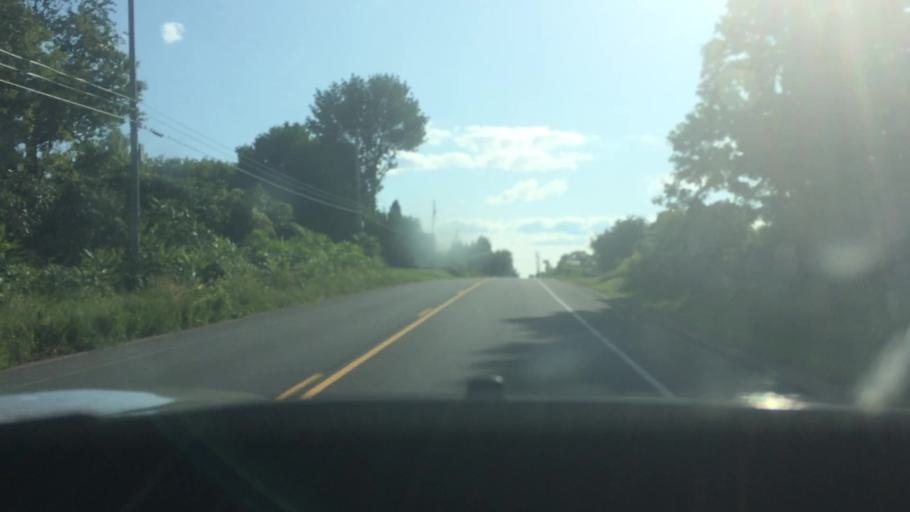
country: US
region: New York
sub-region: Franklin County
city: Malone
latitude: 44.7710
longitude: -74.5164
